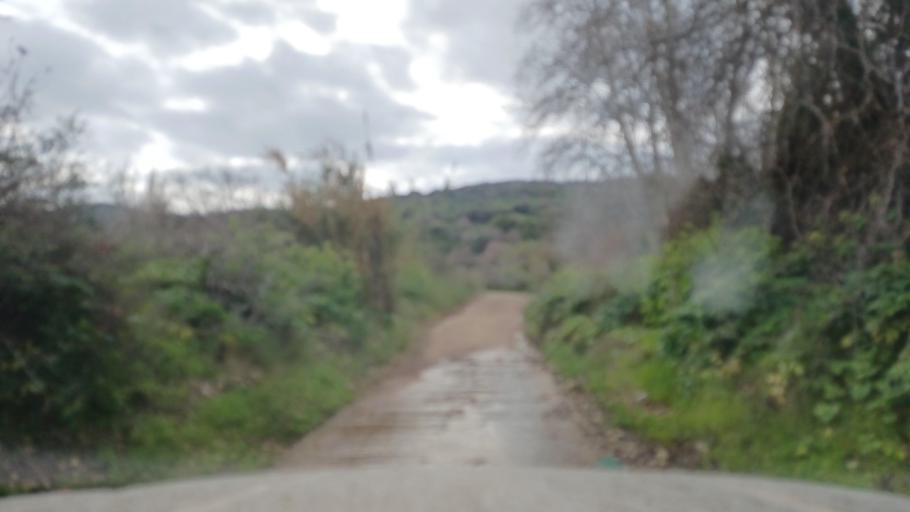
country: CY
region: Limassol
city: Pissouri
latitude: 34.7759
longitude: 32.6619
